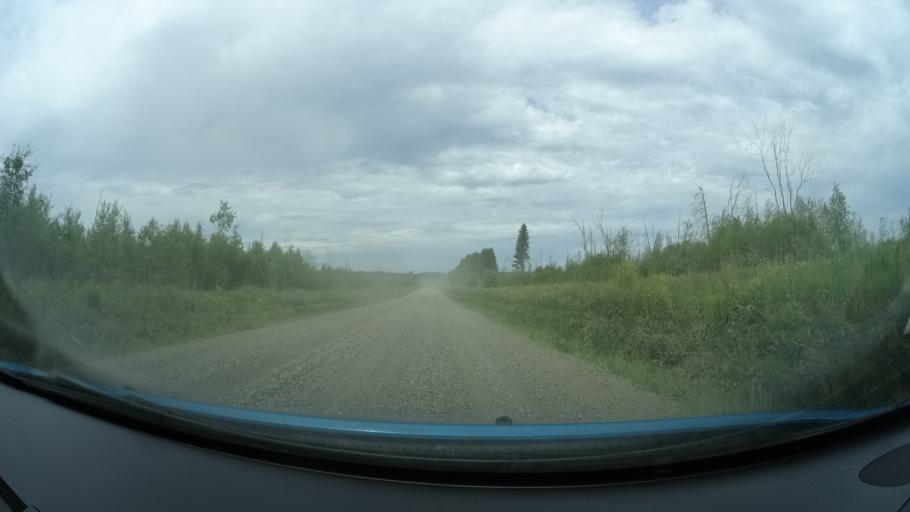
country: RU
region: Perm
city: Barda
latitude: 56.7921
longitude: 55.6756
